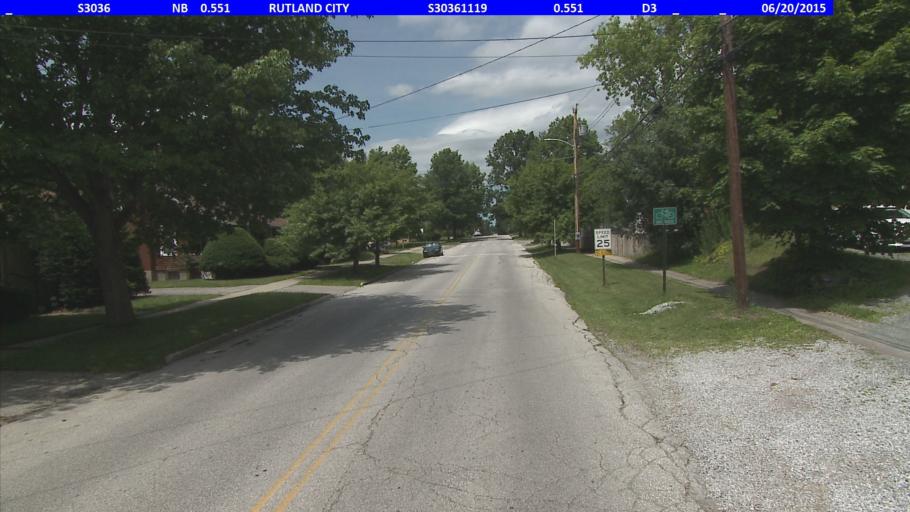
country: US
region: Vermont
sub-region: Rutland County
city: Rutland
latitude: 43.6162
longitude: -72.9770
